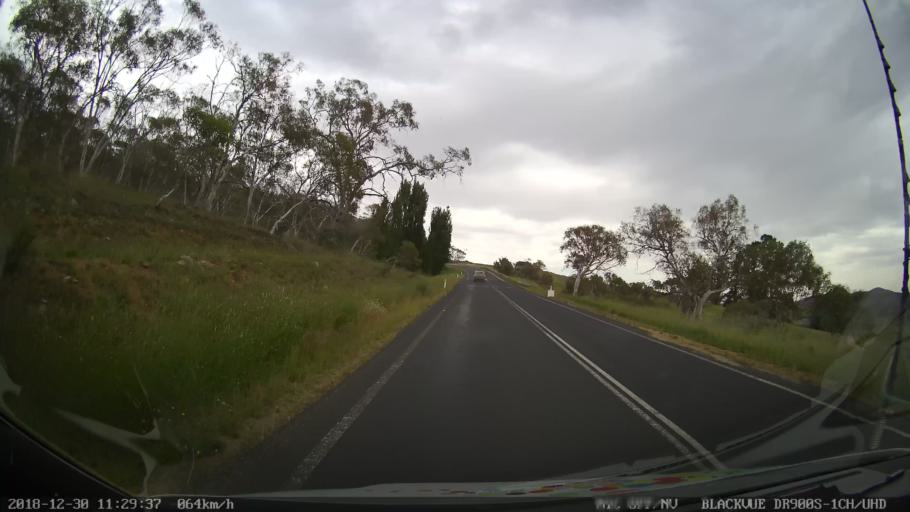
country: AU
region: New South Wales
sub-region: Snowy River
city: Jindabyne
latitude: -36.4489
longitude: 148.6095
